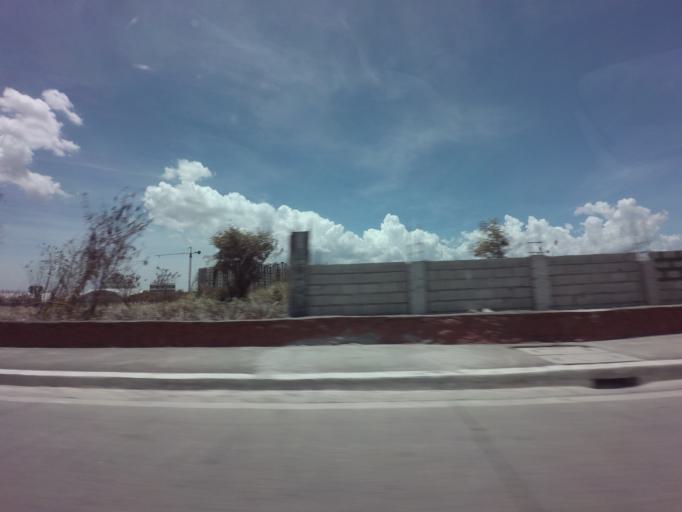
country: PH
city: Sambayanihan People's Village
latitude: 14.4863
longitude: 120.9957
